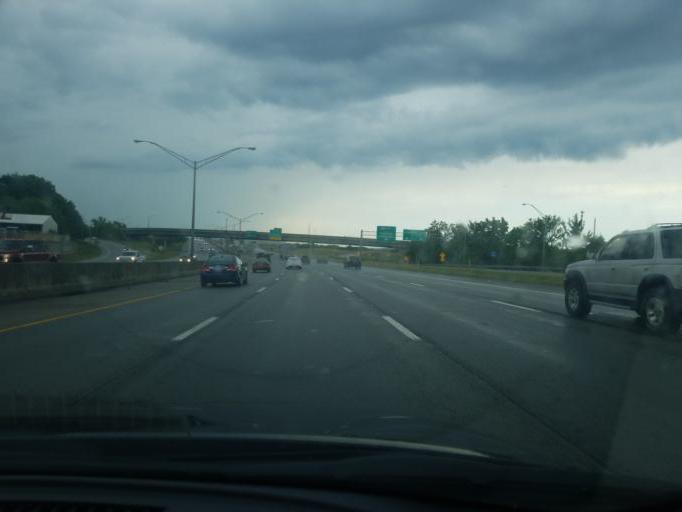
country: US
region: Kentucky
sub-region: Jefferson County
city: Audubon Park
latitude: 38.1950
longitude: -85.7333
